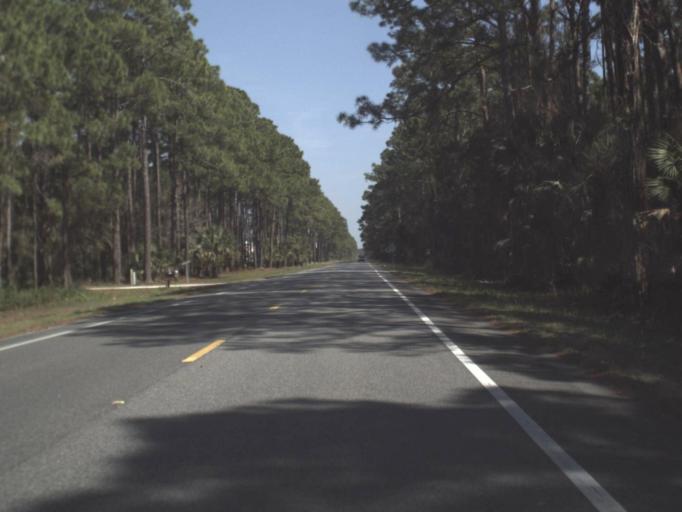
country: US
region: Florida
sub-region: Franklin County
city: Apalachicola
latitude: 29.7164
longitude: -85.0427
